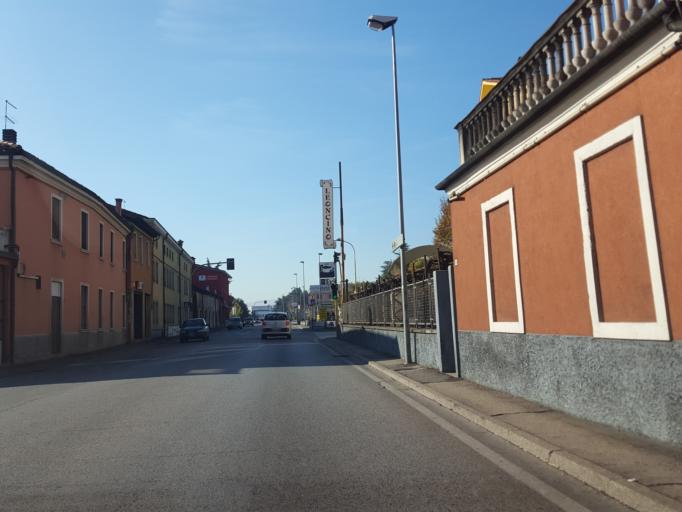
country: IT
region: Veneto
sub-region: Provincia di Vicenza
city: Tavernelle
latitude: 45.5133
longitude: 11.4550
